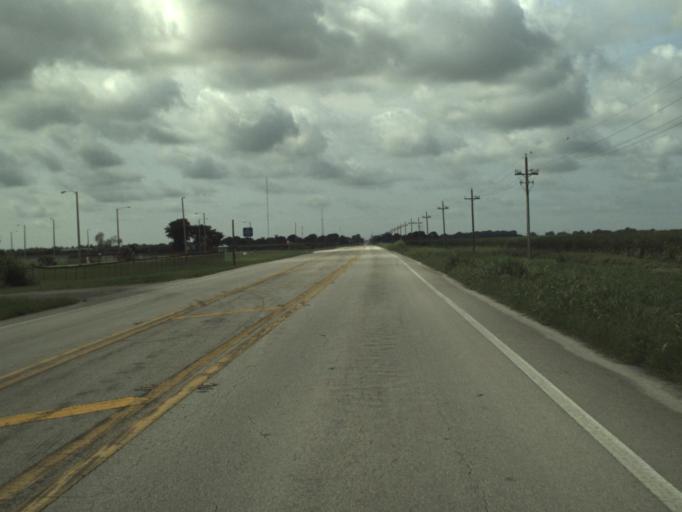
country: US
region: Florida
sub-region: Palm Beach County
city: Belle Glade
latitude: 26.7228
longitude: -80.6841
